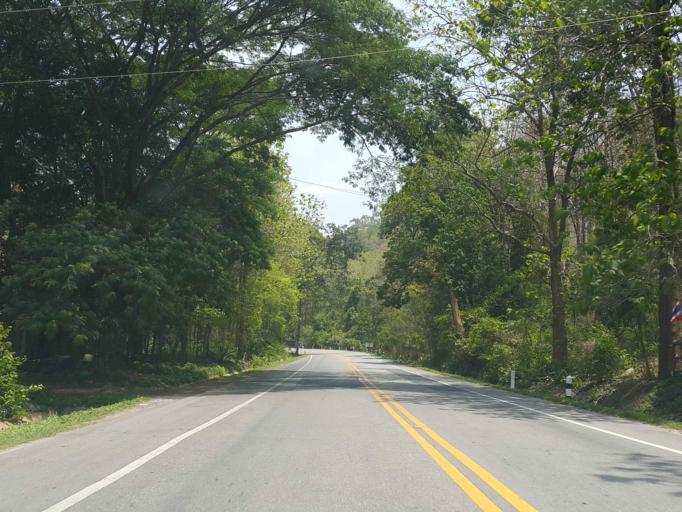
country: TH
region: Chiang Mai
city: Mae On
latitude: 18.9358
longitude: 99.2383
